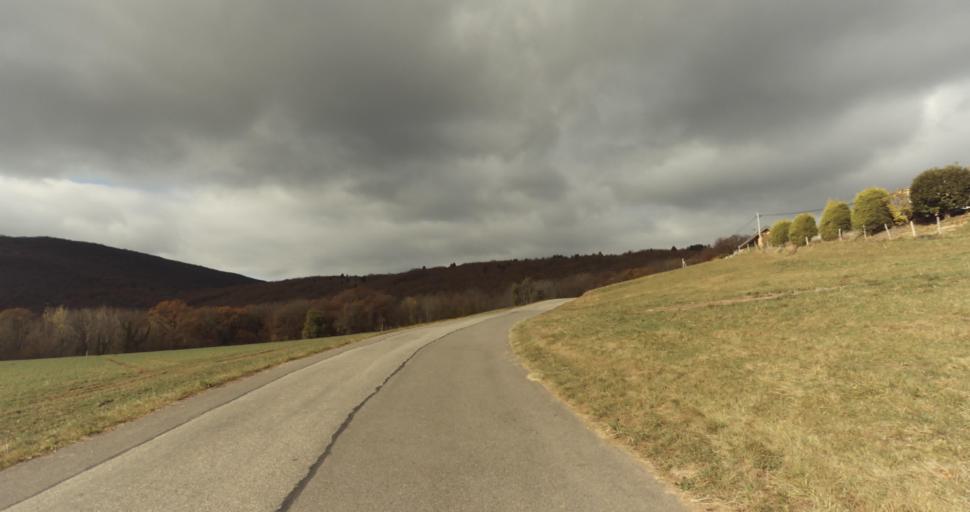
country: FR
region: Rhone-Alpes
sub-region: Departement de la Haute-Savoie
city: Epagny
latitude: 45.9564
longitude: 6.0769
